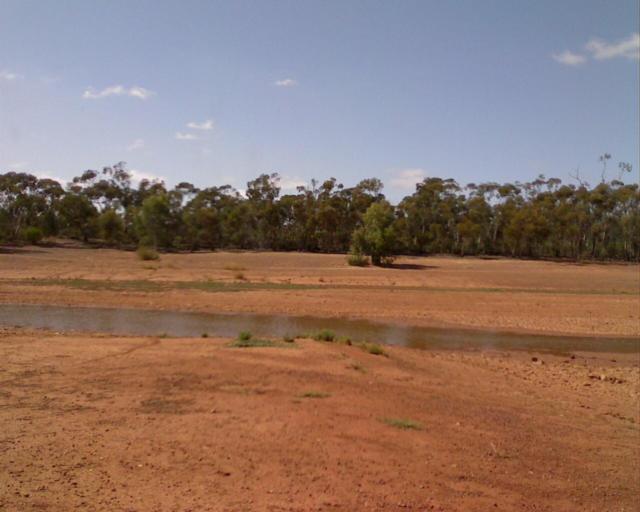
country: AU
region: Western Australia
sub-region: Kalgoorlie/Boulder
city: Boulder
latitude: -30.8456
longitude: 121.3899
